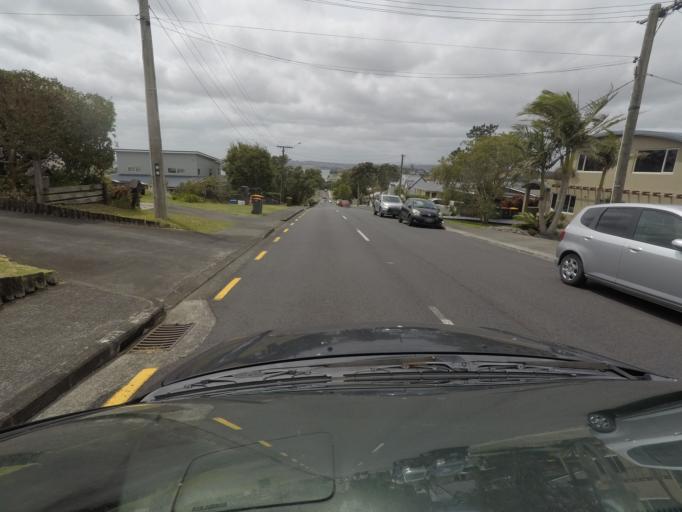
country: NZ
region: Auckland
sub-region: Auckland
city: Pakuranga
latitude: -36.8891
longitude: 174.9326
